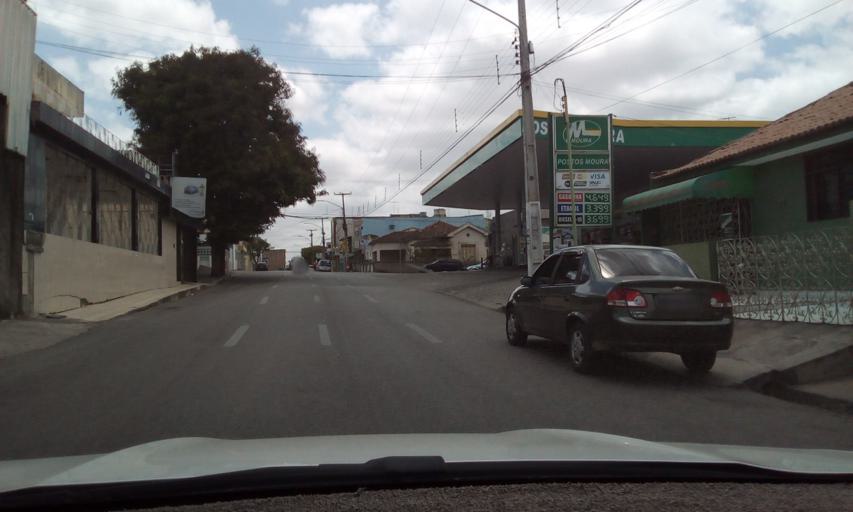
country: BR
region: Pernambuco
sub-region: Caruaru
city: Caruaru
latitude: -8.2889
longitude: -35.9819
